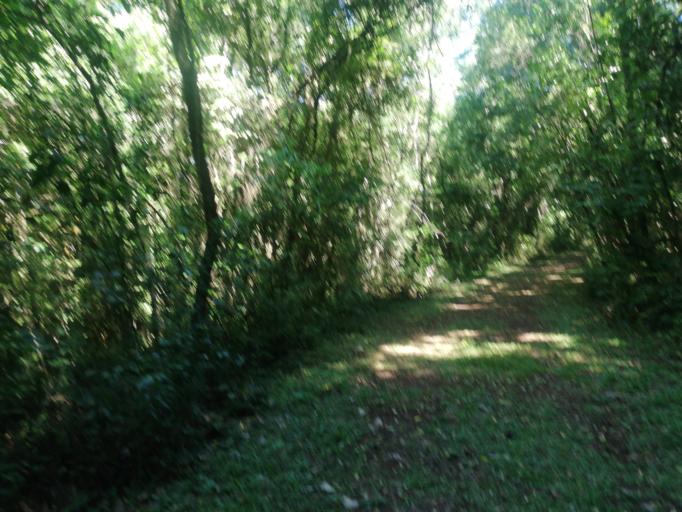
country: AR
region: Misiones
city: Cerro Azul
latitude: -27.7466
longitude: -55.5608
